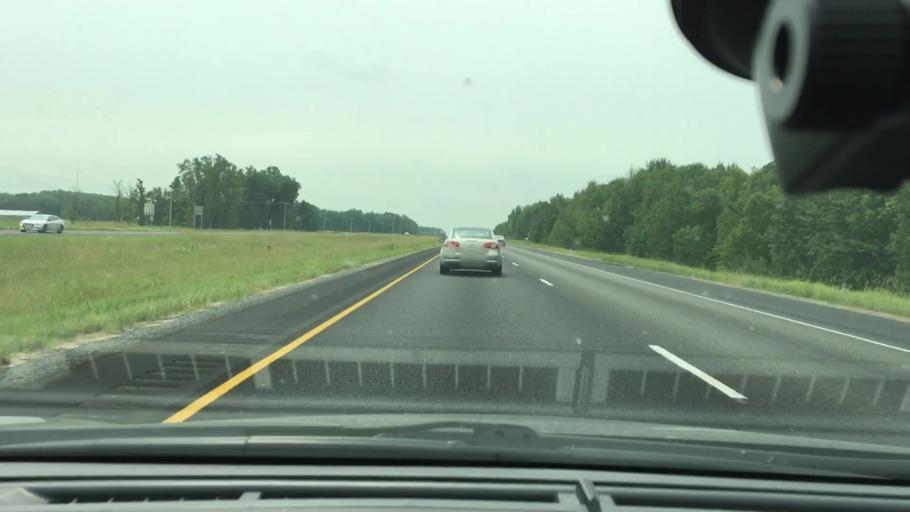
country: US
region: Minnesota
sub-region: Mille Lacs County
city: Milaca
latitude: 45.9221
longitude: -93.6635
